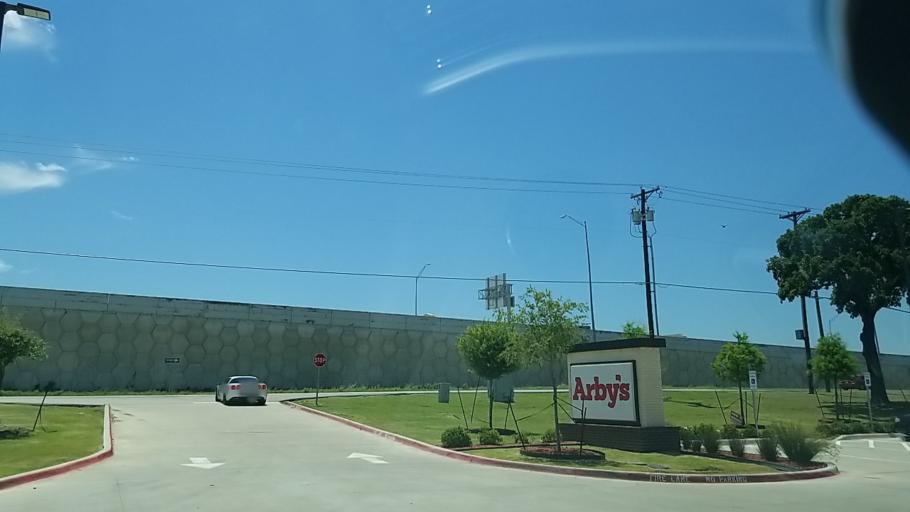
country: US
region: Texas
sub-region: Denton County
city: Hickory Creek
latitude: 33.1312
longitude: -97.0396
